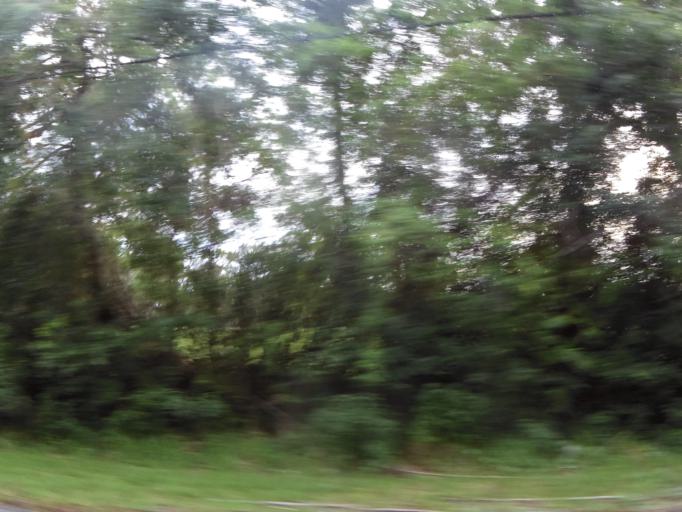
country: US
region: Florida
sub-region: Duval County
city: Jacksonville
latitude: 30.3962
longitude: -81.6965
